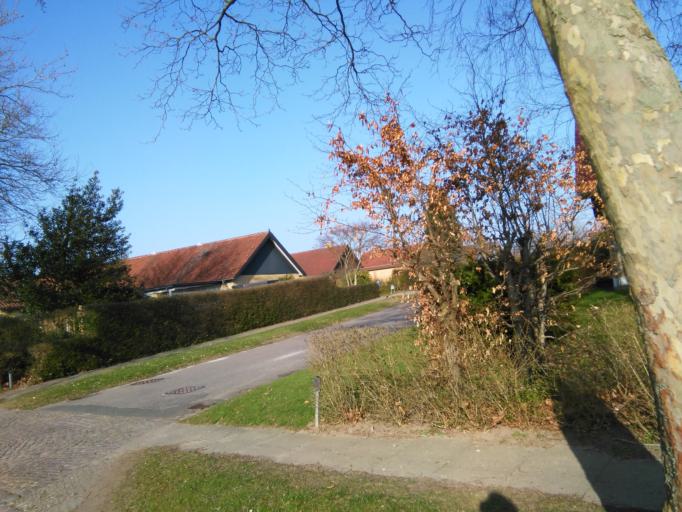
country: DK
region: Central Jutland
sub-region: Arhus Kommune
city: Beder
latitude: 56.0638
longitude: 10.2114
